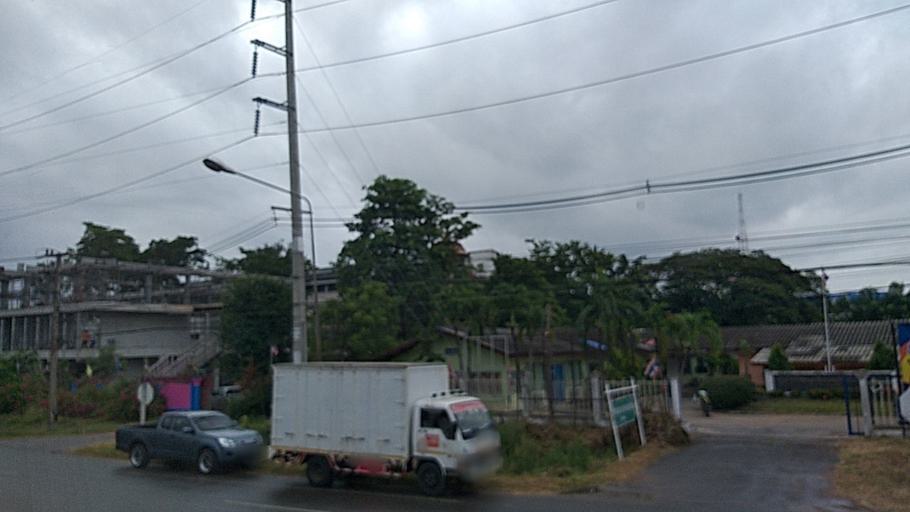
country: TH
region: Maha Sarakham
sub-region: Amphoe Borabue
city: Borabue
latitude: 16.0437
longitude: 103.1247
